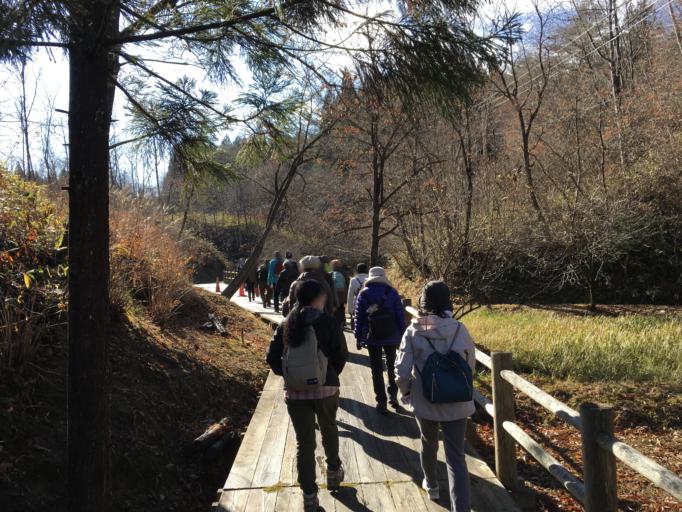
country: JP
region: Iwate
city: Ichinoseki
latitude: 38.9962
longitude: 141.0970
